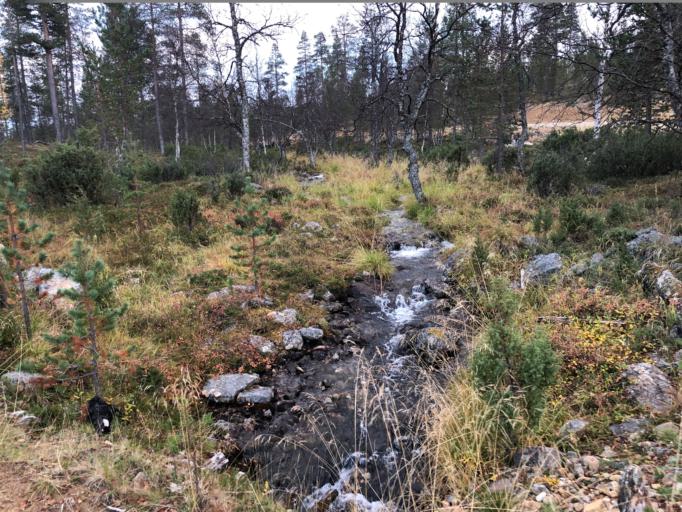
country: FI
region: Lapland
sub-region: Pohjois-Lappi
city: Ivalo
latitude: 68.5641
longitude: 27.6383
